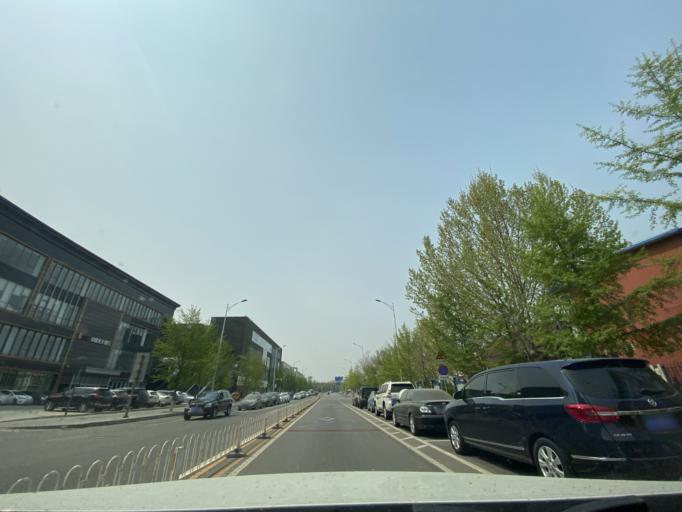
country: CN
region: Beijing
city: Sijiqing
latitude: 39.9399
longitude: 116.2659
